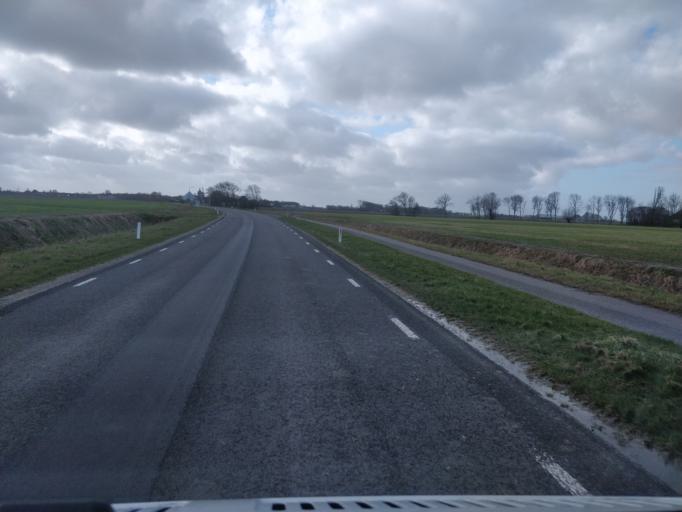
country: NL
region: Friesland
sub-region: Gemeente Franekeradeel
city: Sexbierum
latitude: 53.2284
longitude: 5.4982
